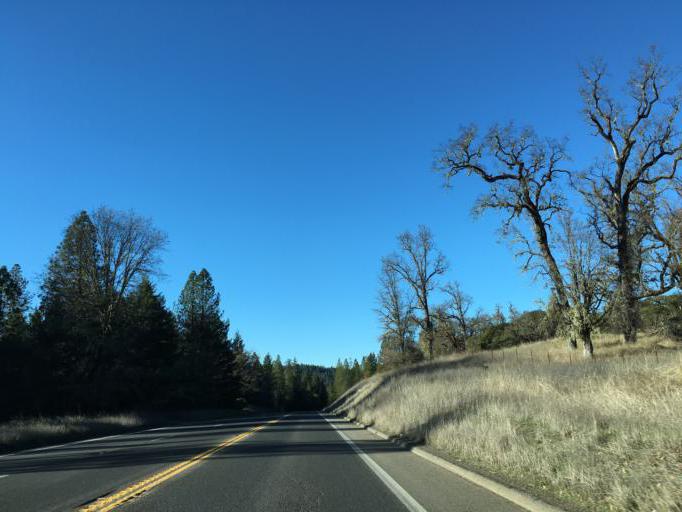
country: US
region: California
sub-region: Mendocino County
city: Laytonville
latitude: 39.7125
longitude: -123.4944
